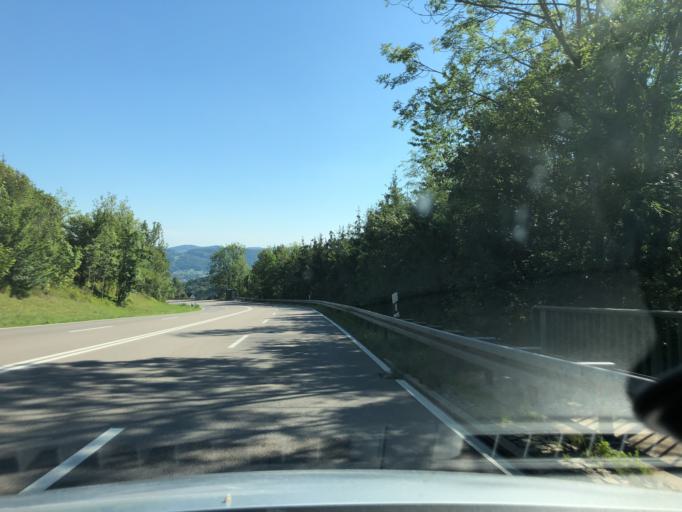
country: DE
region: Baden-Wuerttemberg
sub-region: Freiburg Region
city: Dogern
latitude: 47.6341
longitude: 8.1844
